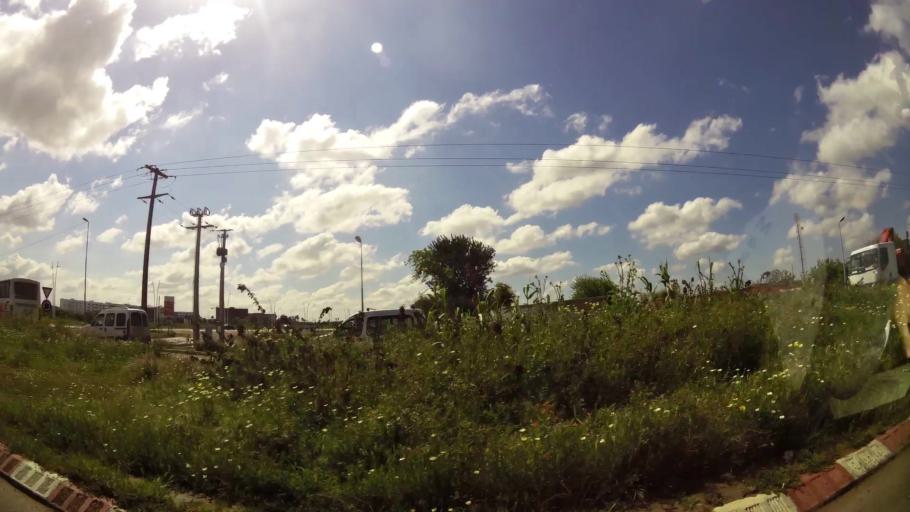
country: MA
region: Grand Casablanca
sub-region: Mediouna
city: Mediouna
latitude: 33.4100
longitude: -7.5331
